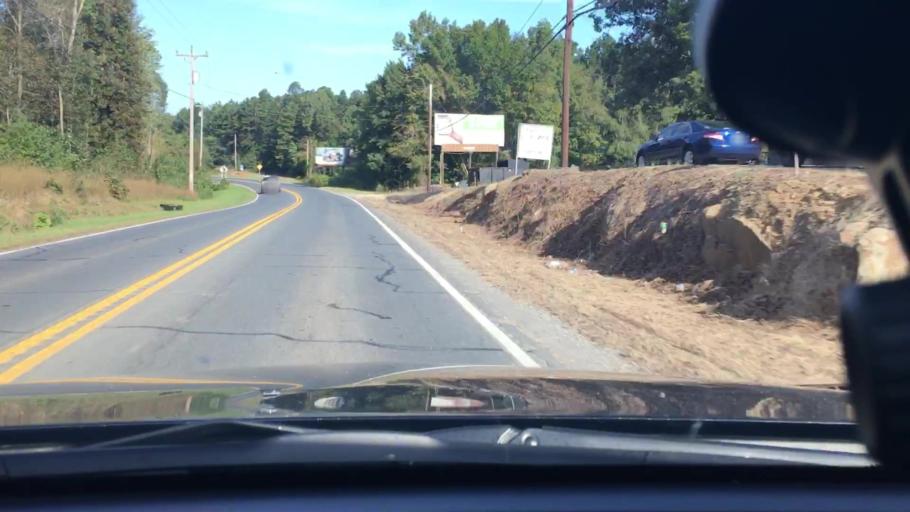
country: US
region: North Carolina
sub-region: Stanly County
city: Albemarle
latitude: 35.3419
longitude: -80.1403
